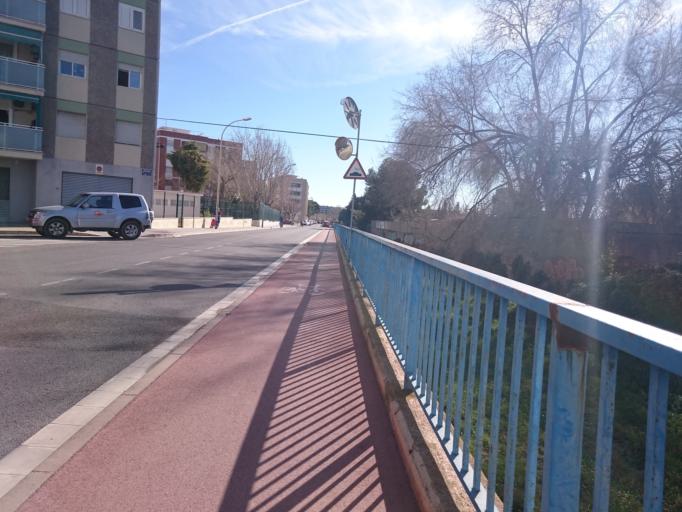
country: ES
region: Catalonia
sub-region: Provincia de Barcelona
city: Vilanova i la Geltru
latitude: 41.2183
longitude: 1.7184
